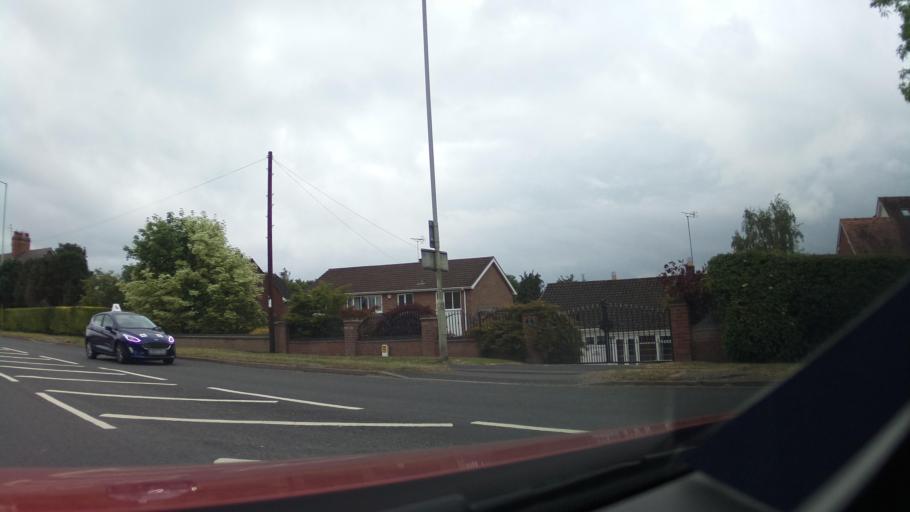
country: GB
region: England
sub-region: Staffordshire
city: Penkridge
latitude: 52.7221
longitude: -2.1168
